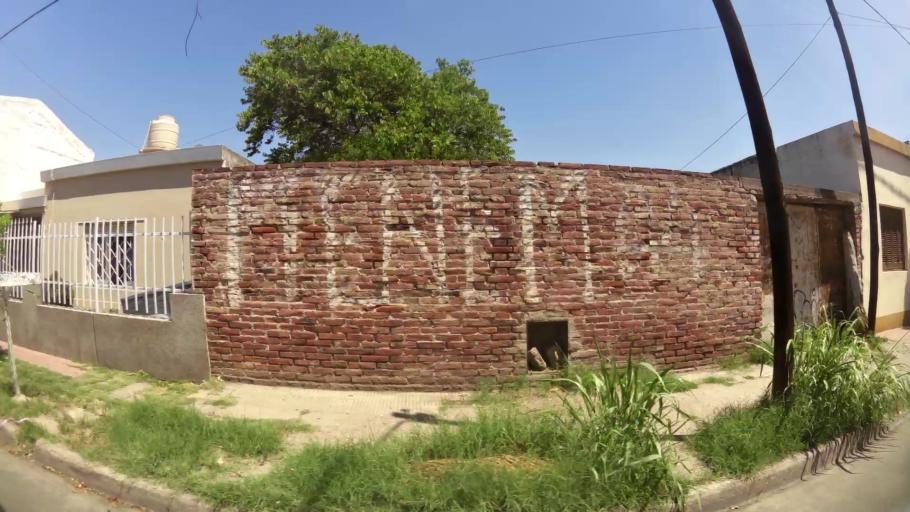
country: AR
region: Cordoba
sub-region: Departamento de Capital
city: Cordoba
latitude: -31.3782
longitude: -64.2007
